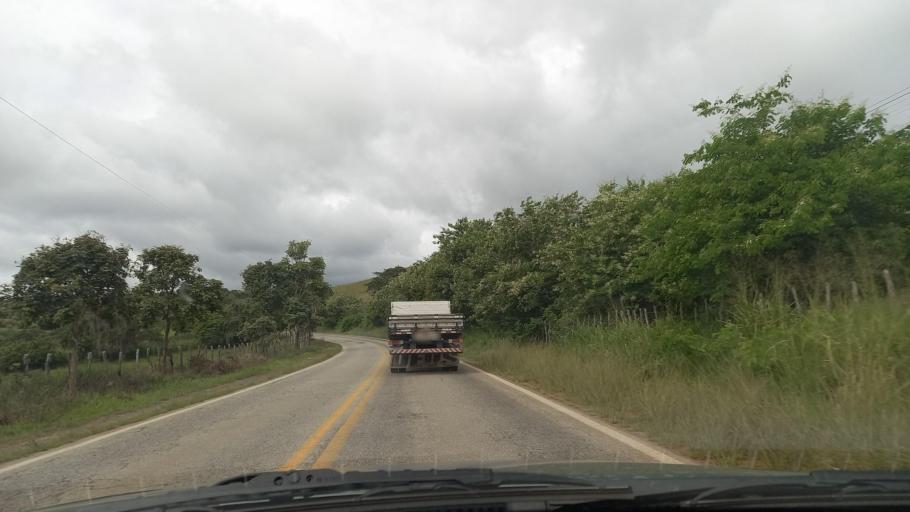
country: BR
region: Pernambuco
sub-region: Canhotinho
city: Canhotinho
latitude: -8.8655
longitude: -36.1871
